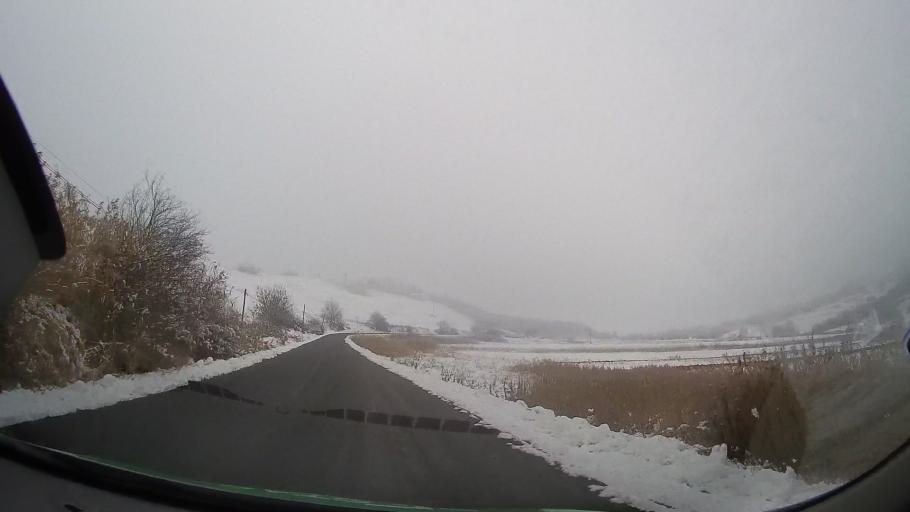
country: RO
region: Bacau
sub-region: Comuna Oncesti
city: Oncesti
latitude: 46.4813
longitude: 27.2571
